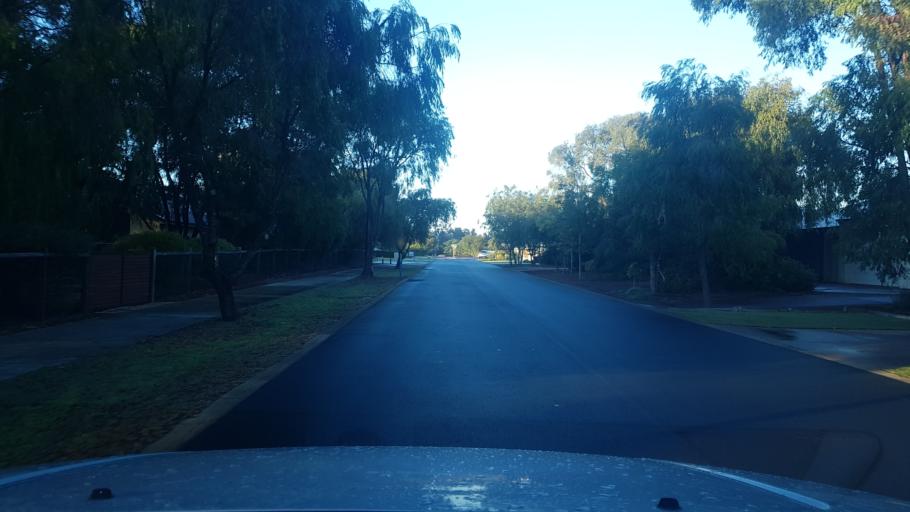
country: AU
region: Western Australia
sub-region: Busselton
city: Vasse
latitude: -33.6625
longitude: 115.2625
